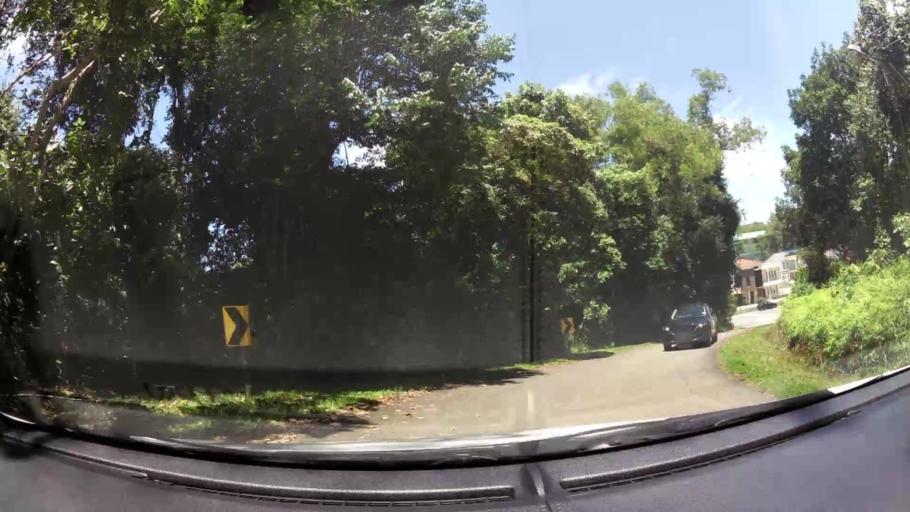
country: BN
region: Brunei and Muara
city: Bandar Seri Begawan
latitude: 4.9298
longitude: 114.9619
